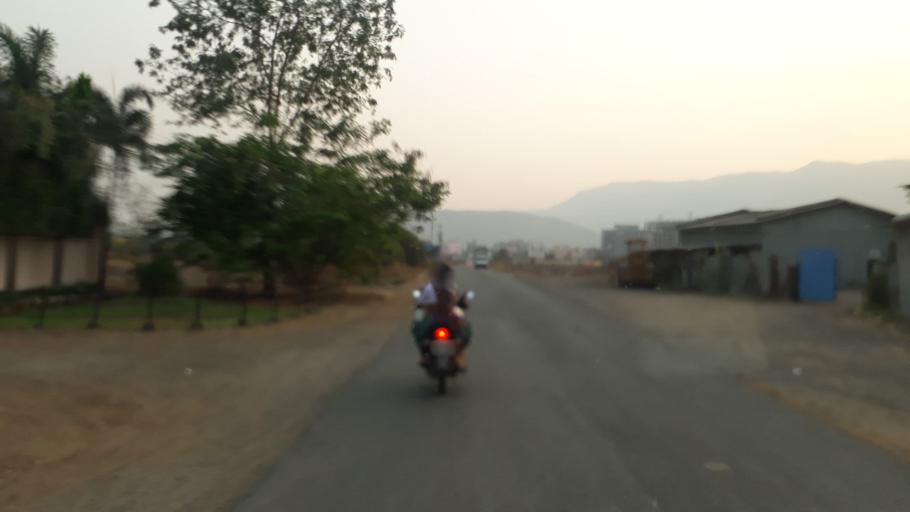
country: IN
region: Maharashtra
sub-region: Raigarh
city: Neral
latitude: 19.0365
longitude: 73.3279
